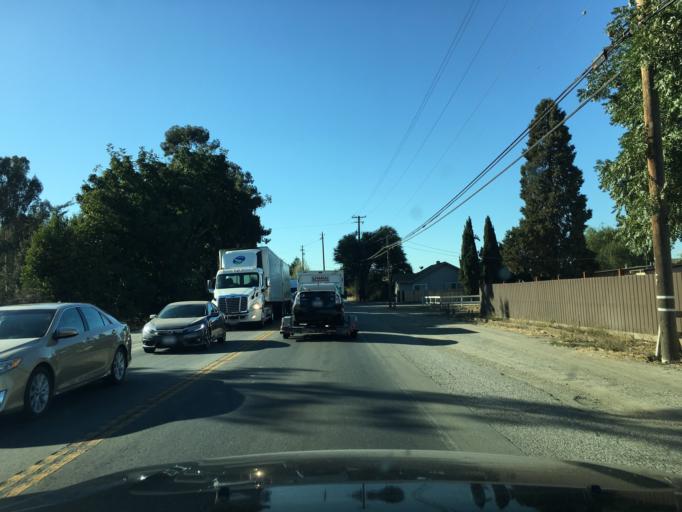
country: US
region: California
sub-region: Santa Clara County
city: Gilroy
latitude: 36.9998
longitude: -121.5268
